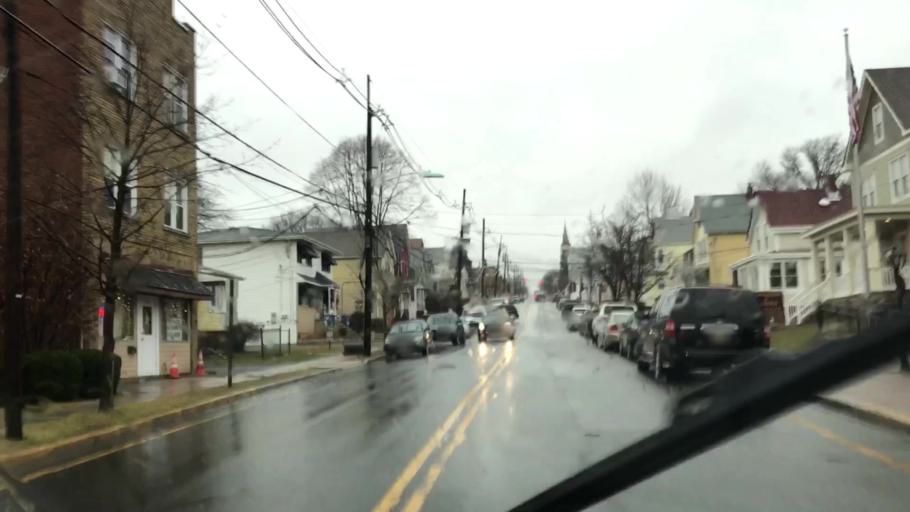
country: US
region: New Jersey
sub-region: Bergen County
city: Garfield
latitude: 40.8731
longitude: -74.1096
